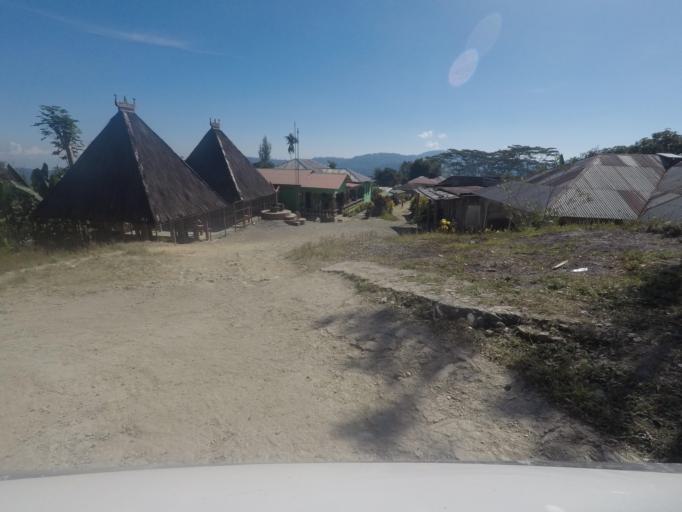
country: TL
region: Ermera
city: Gleno
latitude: -8.7291
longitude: 125.3411
